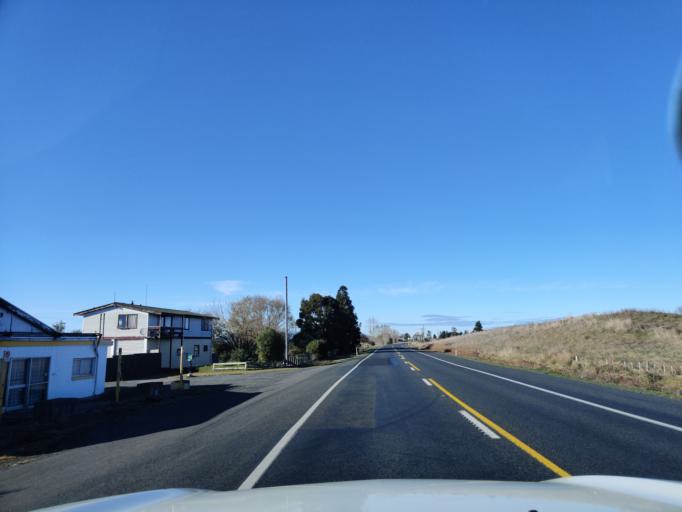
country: NZ
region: Waikato
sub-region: Hauraki District
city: Ngatea
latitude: -37.2981
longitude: 175.5567
